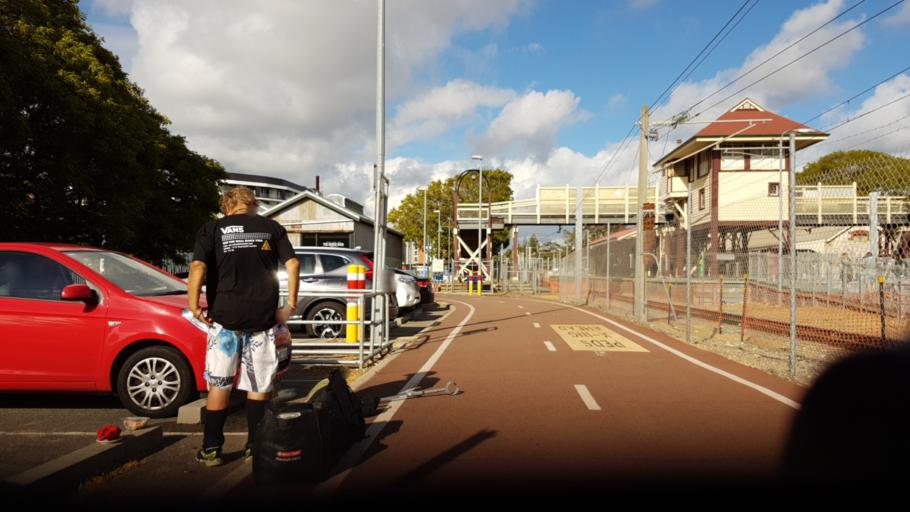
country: AU
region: Western Australia
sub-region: Claremont
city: Claremont
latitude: -31.9810
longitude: 115.7806
